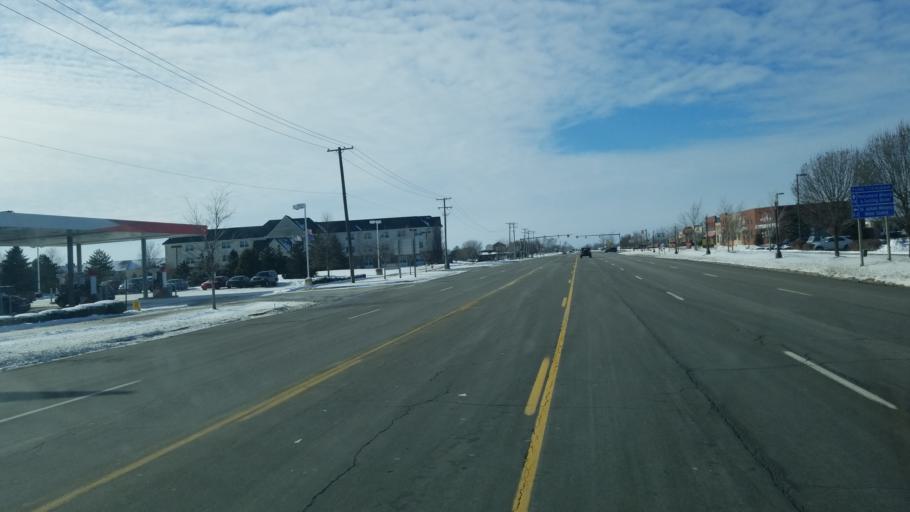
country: US
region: Michigan
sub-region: Monroe County
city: Dundee
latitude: 41.9598
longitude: -83.6747
